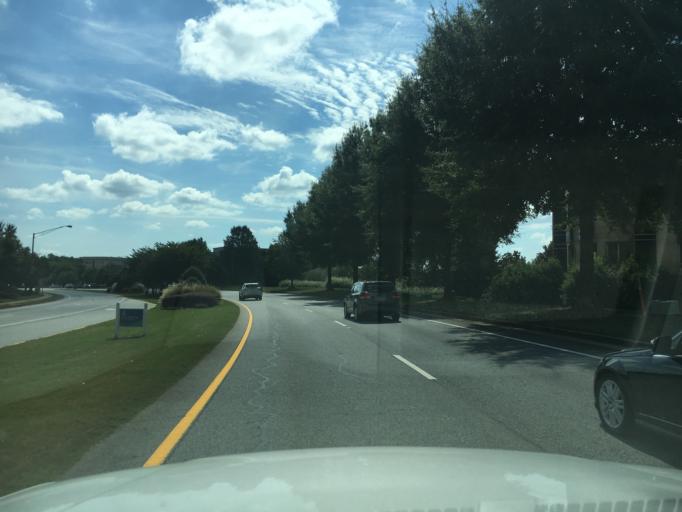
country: US
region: Georgia
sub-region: Gwinnett County
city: Duluth
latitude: 33.9930
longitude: -84.0914
